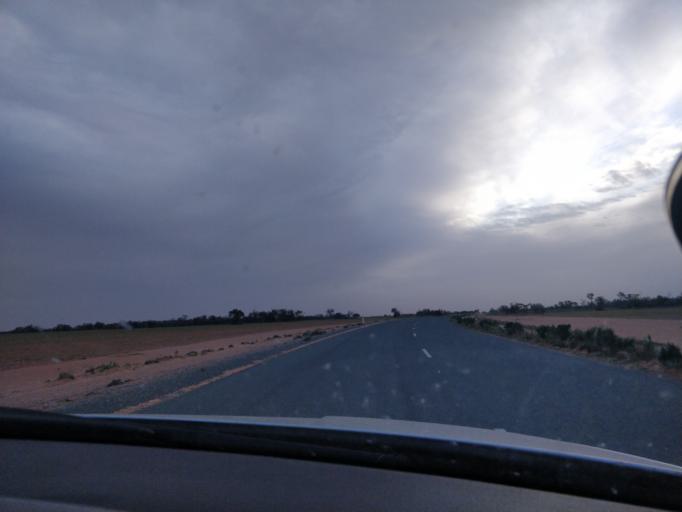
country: AU
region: New South Wales
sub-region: Wentworth
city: Gol Gol
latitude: -34.0364
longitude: 142.3674
